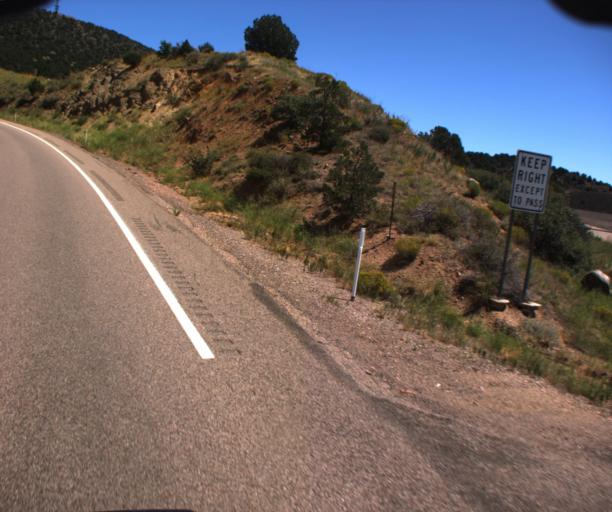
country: US
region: Arizona
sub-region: Gila County
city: San Carlos
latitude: 33.6516
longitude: -110.5697
